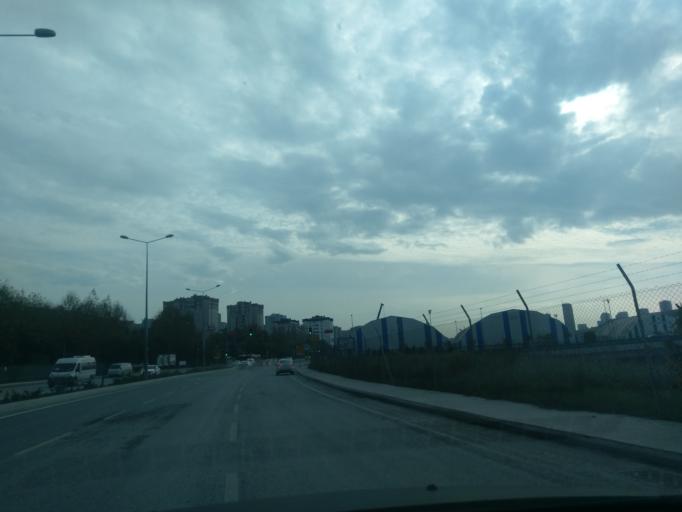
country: TR
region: Istanbul
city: Basaksehir
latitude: 41.0592
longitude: 28.7739
